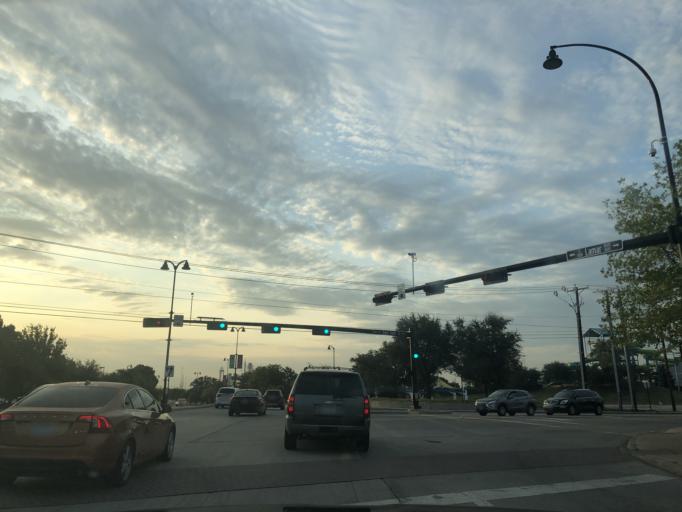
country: US
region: Texas
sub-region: Tarrant County
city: Arlington
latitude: 32.7636
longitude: -97.0856
